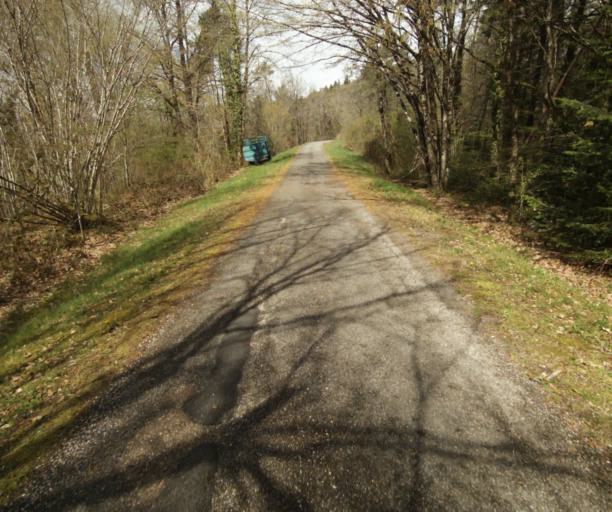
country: FR
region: Limousin
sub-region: Departement de la Correze
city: Sainte-Fortunade
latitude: 45.1789
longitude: 1.8707
